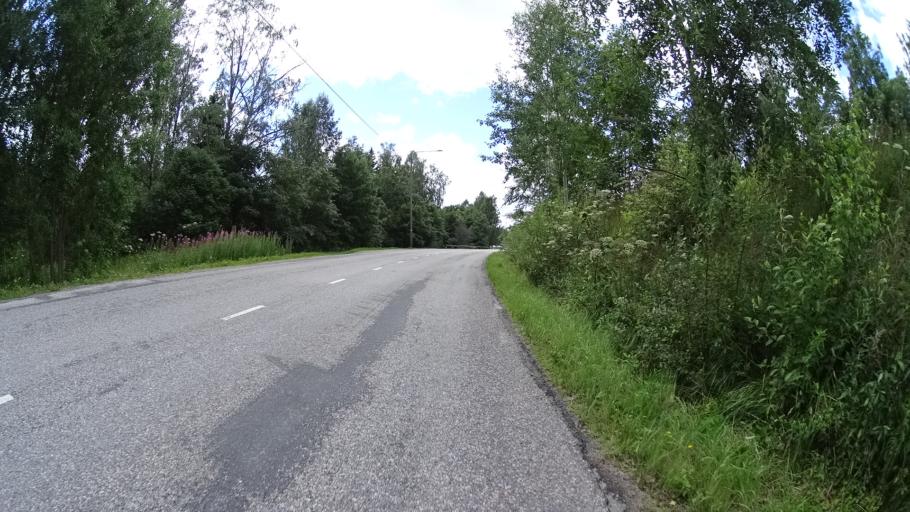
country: FI
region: Uusimaa
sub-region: Helsinki
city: Teekkarikylae
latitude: 60.2945
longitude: 24.8718
